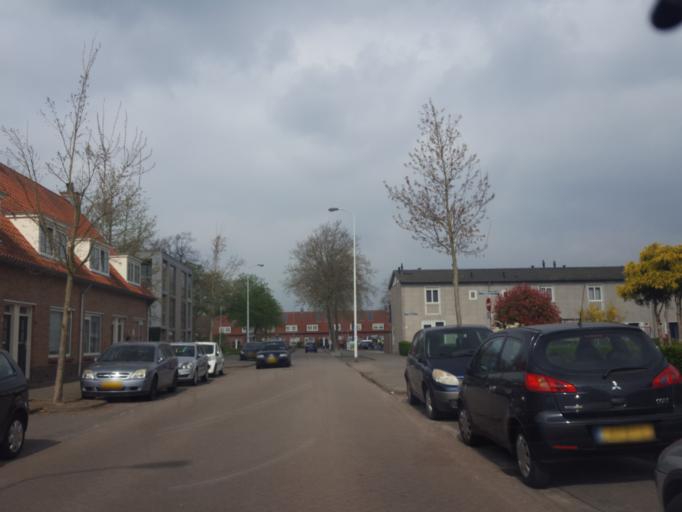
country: NL
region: North Brabant
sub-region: Gemeente Eindhoven
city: Meerhoven
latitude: 51.4411
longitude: 5.4346
